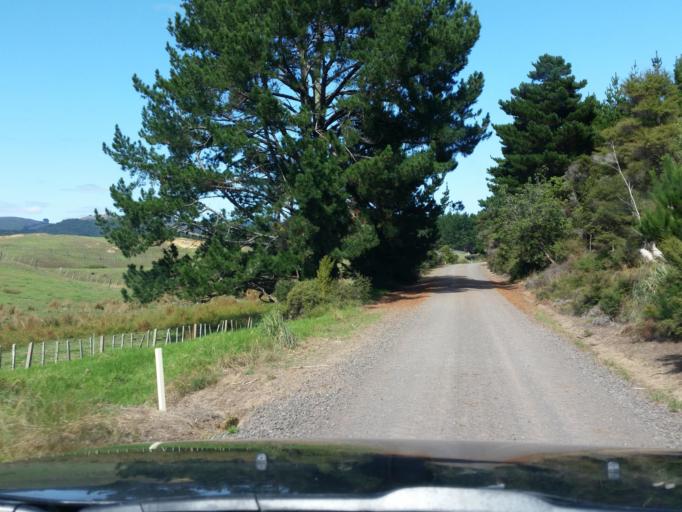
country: NZ
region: Northland
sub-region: Kaipara District
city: Dargaville
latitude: -35.6990
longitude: 173.5220
